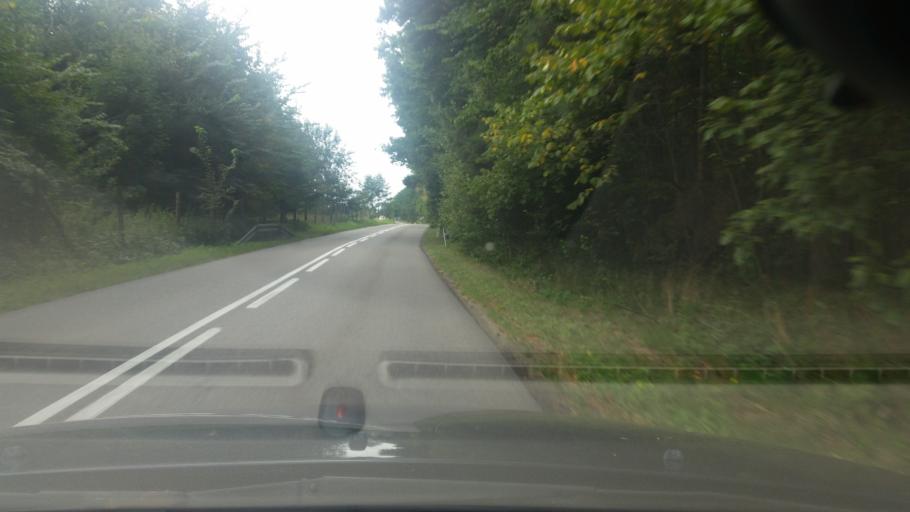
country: PL
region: Pomeranian Voivodeship
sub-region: Powiat leborski
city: Leba
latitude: 54.7399
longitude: 17.6411
